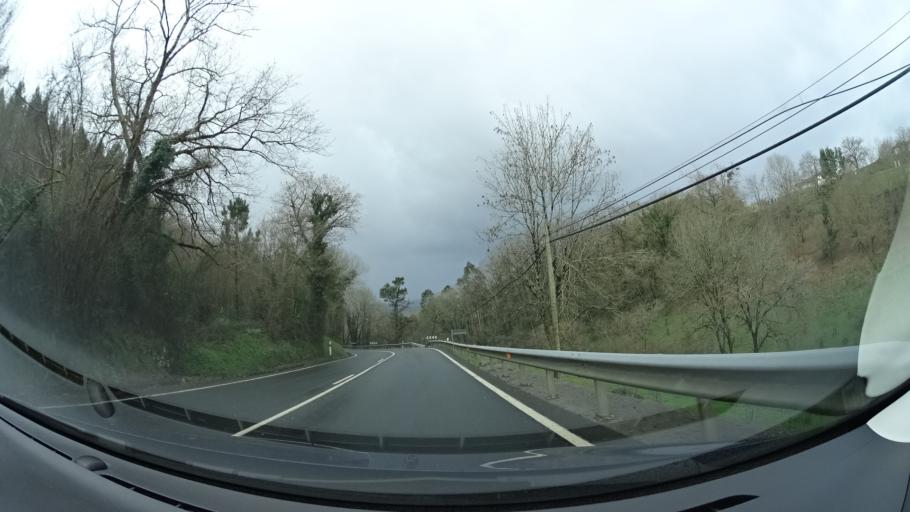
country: ES
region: Basque Country
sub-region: Bizkaia
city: Mungia
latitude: 43.3651
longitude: -2.8275
